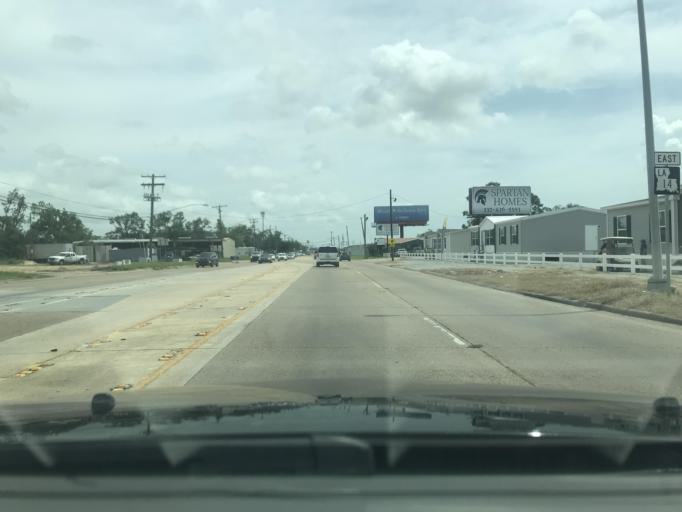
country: US
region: Louisiana
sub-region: Calcasieu Parish
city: Lake Charles
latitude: 30.2345
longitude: -93.1804
